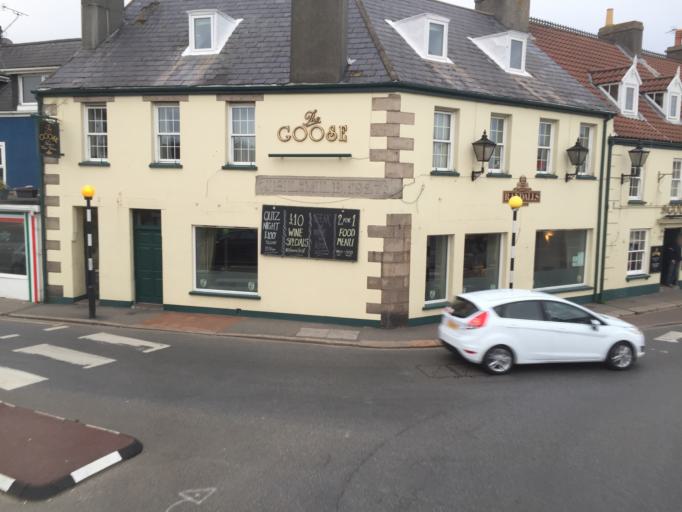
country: JE
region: St Helier
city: Saint Helier
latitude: 49.1965
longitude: -2.1587
